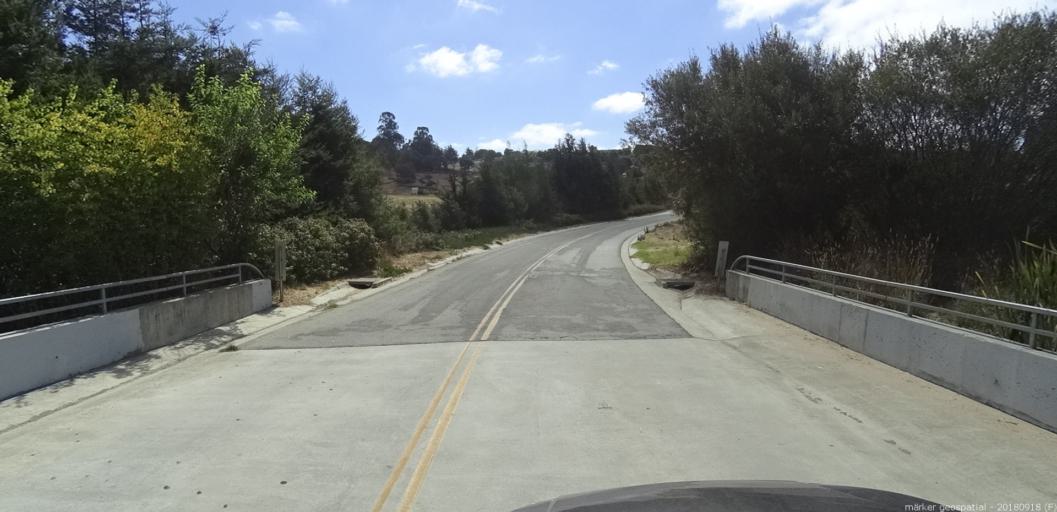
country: US
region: California
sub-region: Monterey County
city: Prunedale
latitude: 36.7672
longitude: -121.6652
